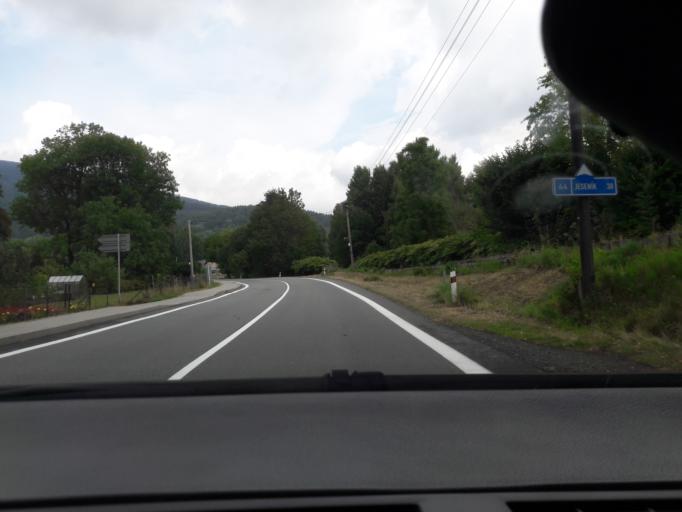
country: CZ
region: Olomoucky
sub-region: Okres Sumperk
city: Loucna nad Desnou
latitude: 50.0874
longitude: 17.0911
